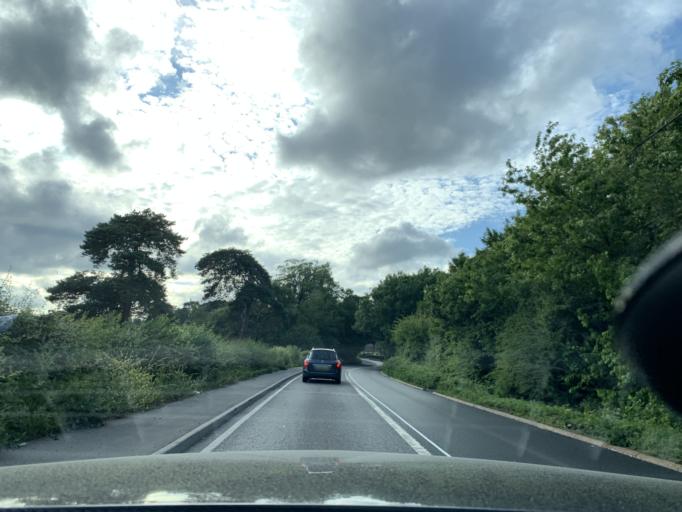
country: GB
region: England
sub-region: East Sussex
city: Battle
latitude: 50.9549
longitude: 0.4999
